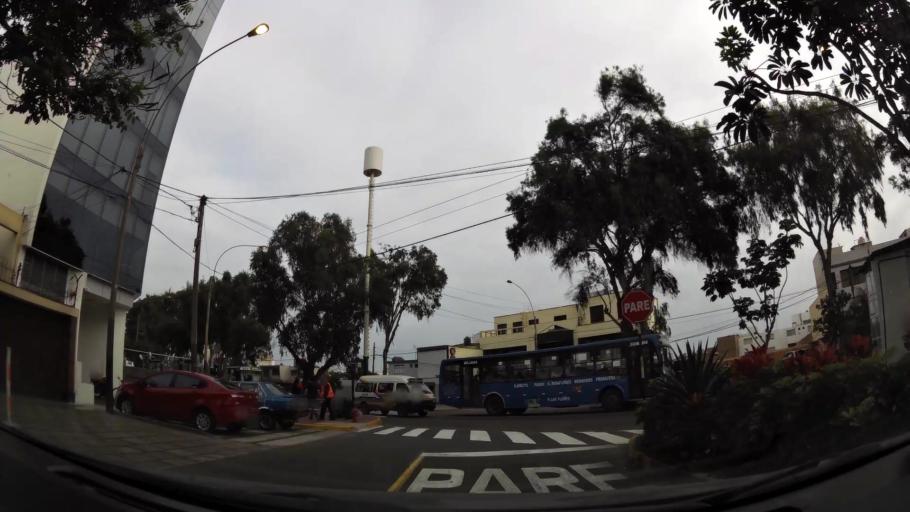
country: PE
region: Lima
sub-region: Lima
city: San Isidro
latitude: -12.1051
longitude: -77.0560
